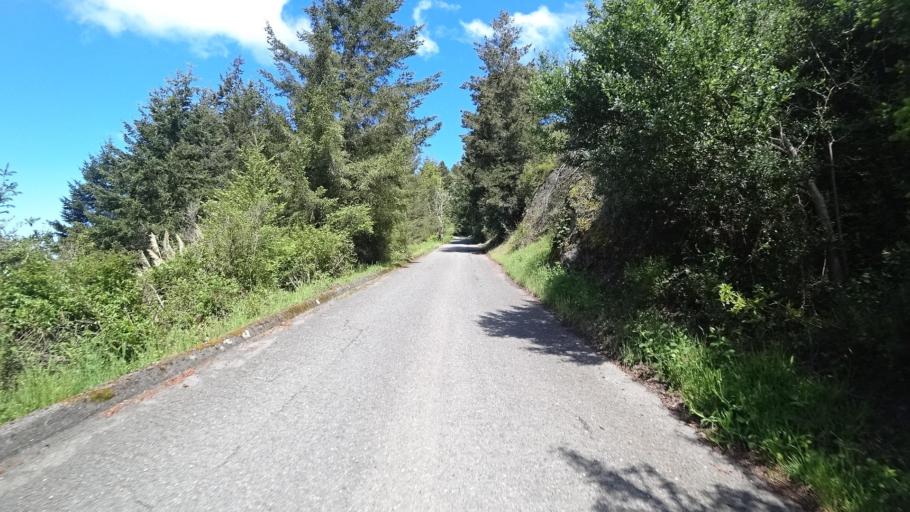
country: US
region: California
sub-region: Humboldt County
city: Arcata
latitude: 40.9087
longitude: -124.0445
